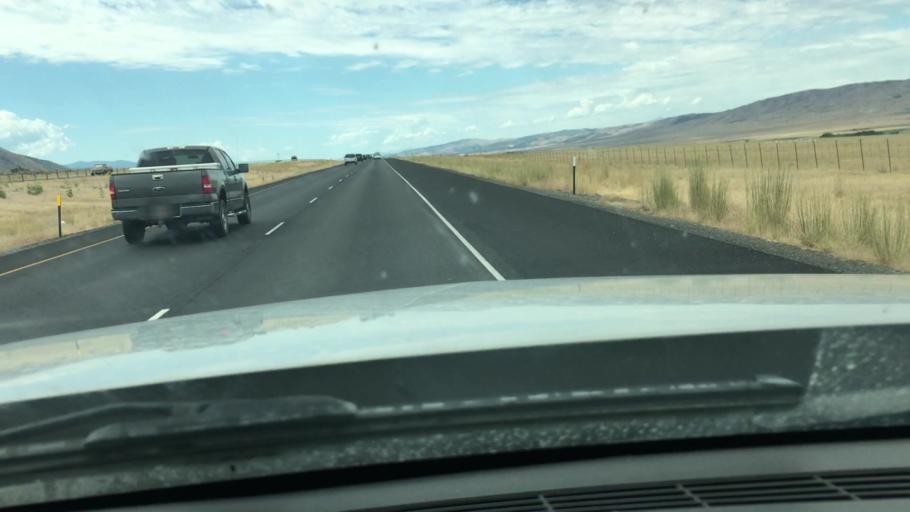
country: US
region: Utah
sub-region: Juab County
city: Mona
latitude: 39.8617
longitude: -111.8324
